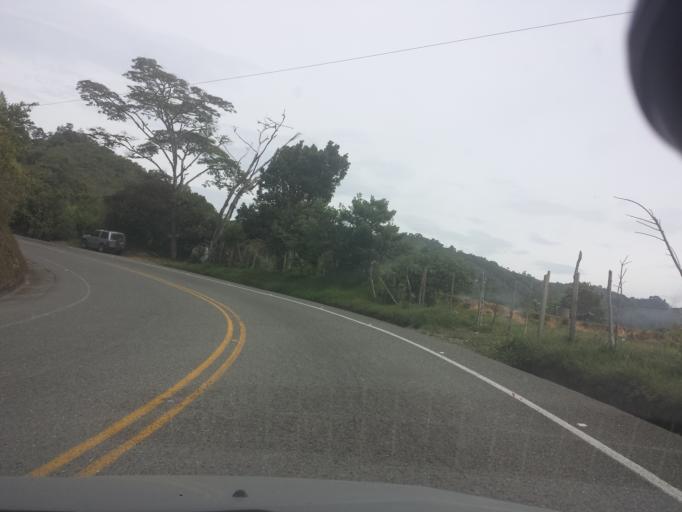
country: CO
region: Antioquia
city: Liborina
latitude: 6.6389
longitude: -75.8717
